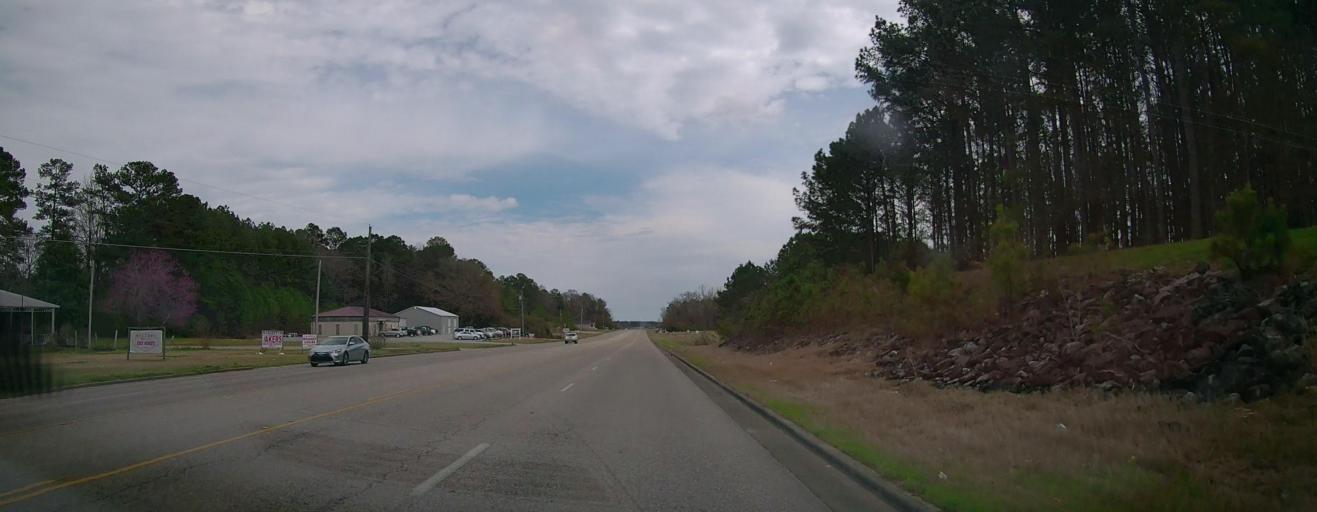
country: US
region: Alabama
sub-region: Marion County
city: Winfield
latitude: 33.9506
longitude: -87.8638
